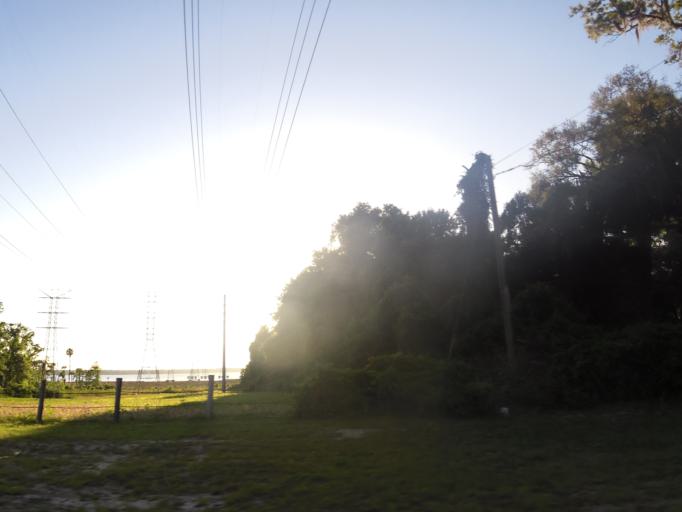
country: US
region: Florida
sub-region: Duval County
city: Atlantic Beach
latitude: 30.3684
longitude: -81.5154
